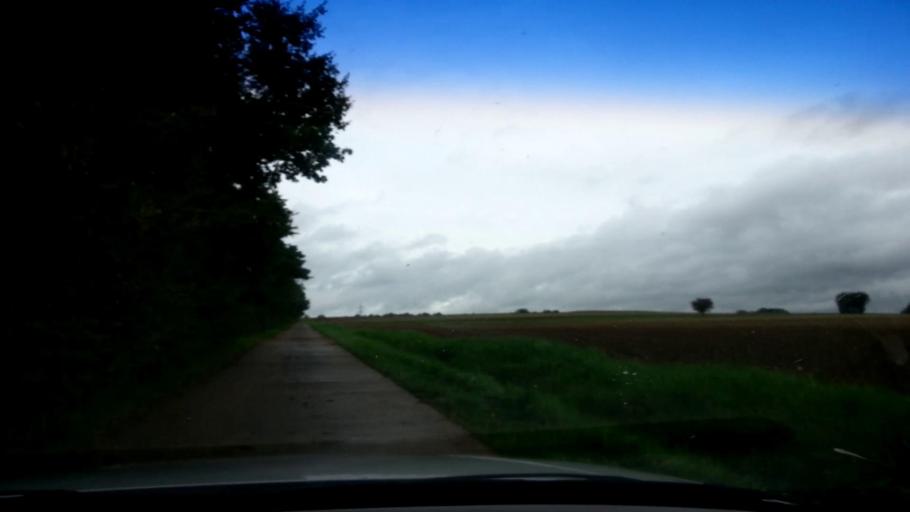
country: DE
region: Bavaria
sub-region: Upper Franconia
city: Memmelsdorf
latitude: 49.9491
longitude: 10.9808
